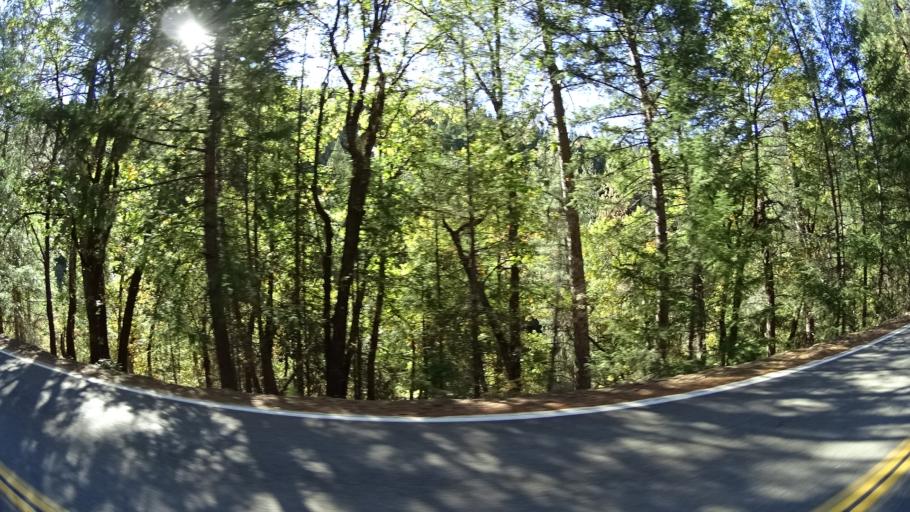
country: US
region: California
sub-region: Trinity County
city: Weaverville
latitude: 41.1546
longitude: -123.1085
